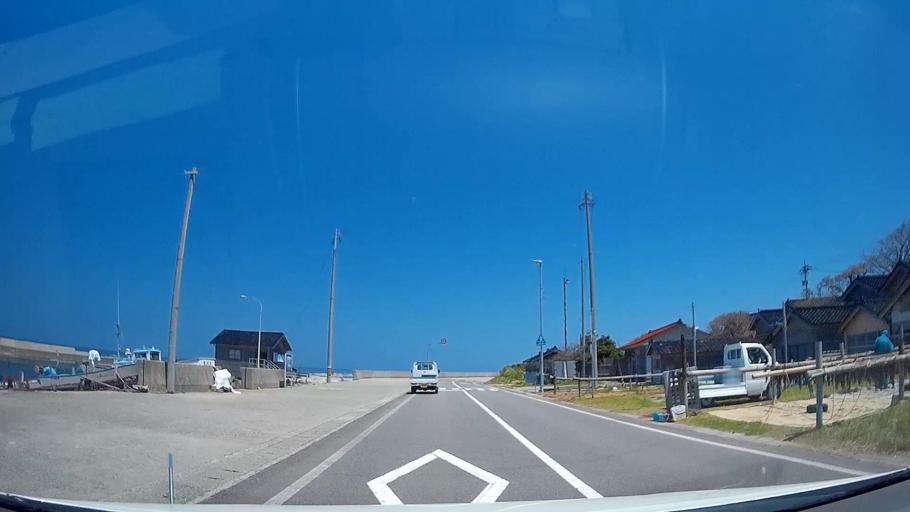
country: JP
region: Ishikawa
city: Nanao
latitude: 37.5289
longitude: 137.2878
